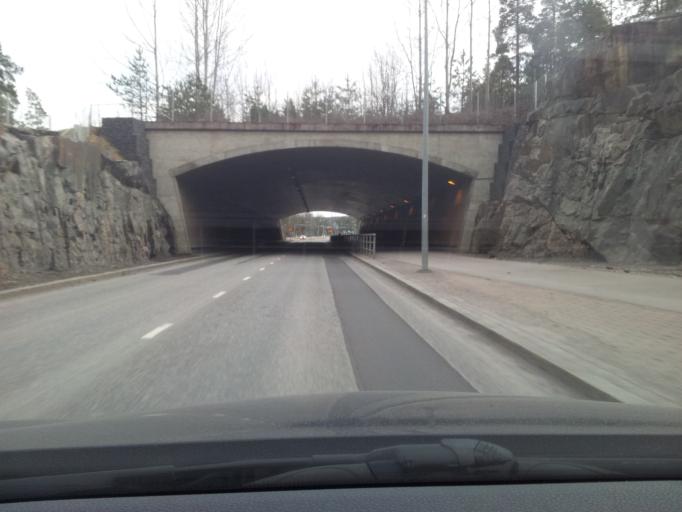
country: FI
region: Uusimaa
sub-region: Helsinki
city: Espoo
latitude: 60.1584
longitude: 24.6603
